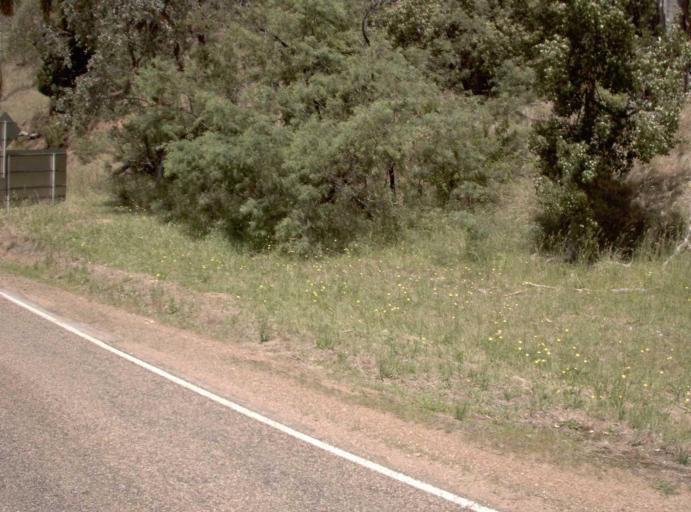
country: AU
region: Victoria
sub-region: East Gippsland
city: Bairnsdale
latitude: -37.3703
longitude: 147.8365
